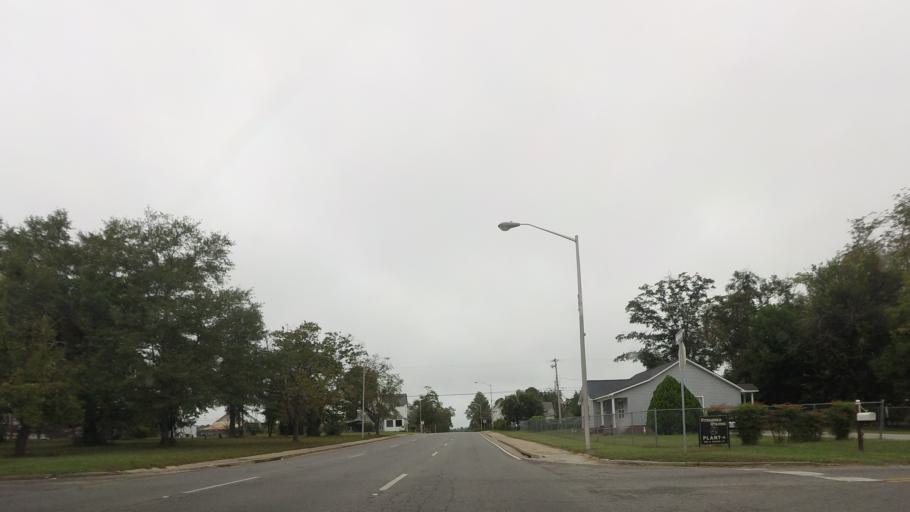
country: US
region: Georgia
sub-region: Ben Hill County
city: Fitzgerald
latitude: 31.7173
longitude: -83.2516
